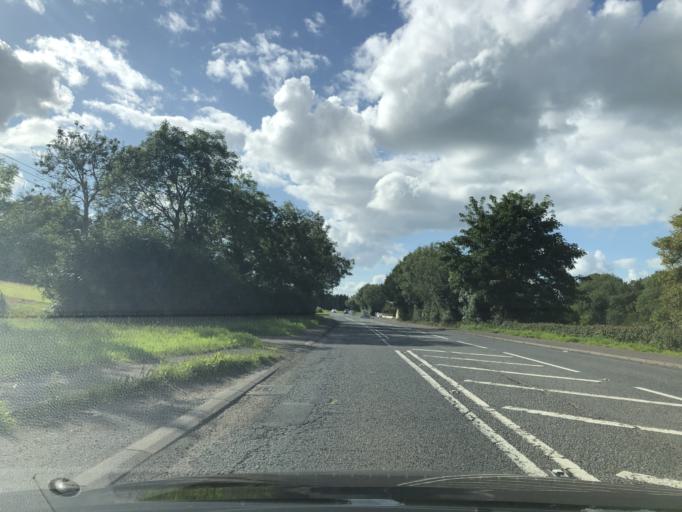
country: GB
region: Northern Ireland
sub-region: Ards District
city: Comber
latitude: 54.5688
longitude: -5.7702
